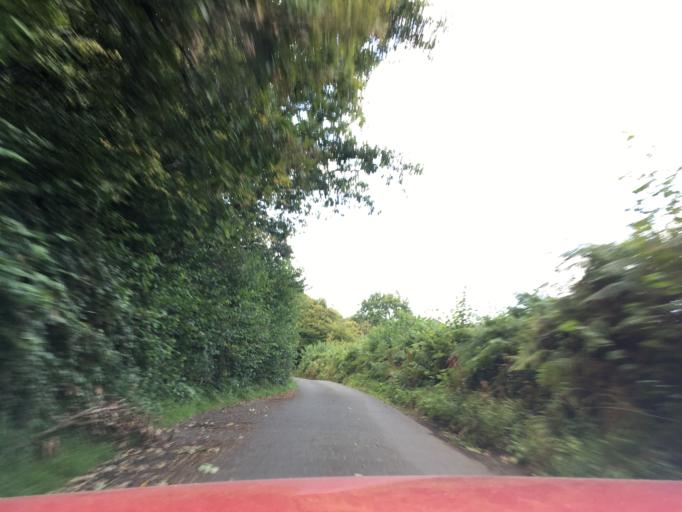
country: GB
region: Wales
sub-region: Cardiff
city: Pentyrch
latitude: 51.5571
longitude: -3.2757
